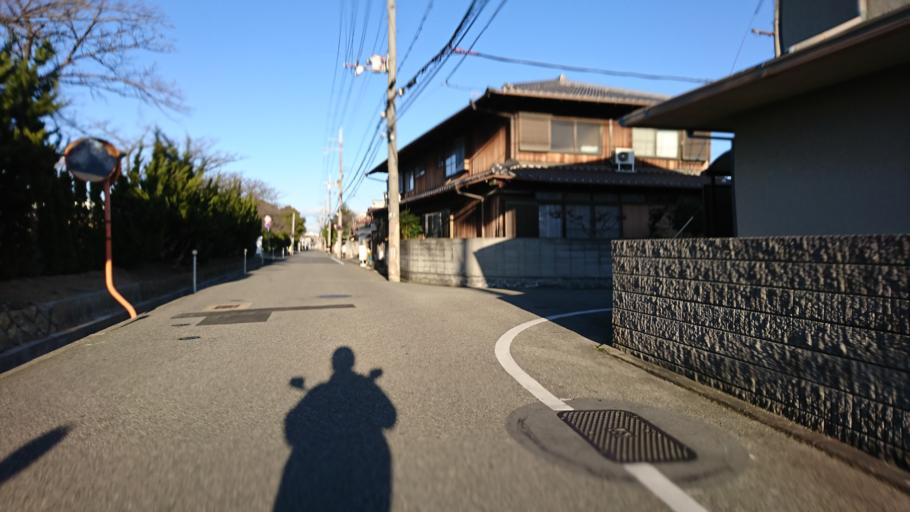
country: JP
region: Hyogo
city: Kakogawacho-honmachi
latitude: 34.7671
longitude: 134.8275
